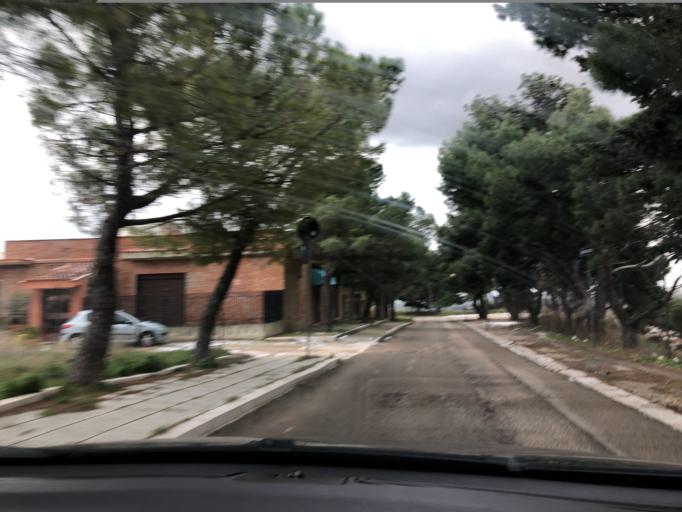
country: IT
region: Apulia
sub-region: Provincia di Foggia
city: Lucera
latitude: 41.5067
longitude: 15.3244
